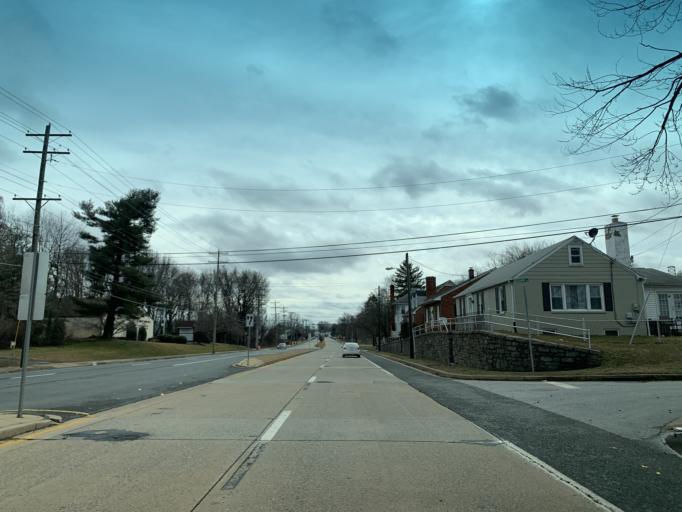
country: US
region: Delaware
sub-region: New Castle County
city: New Castle
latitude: 39.6794
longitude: -75.5596
